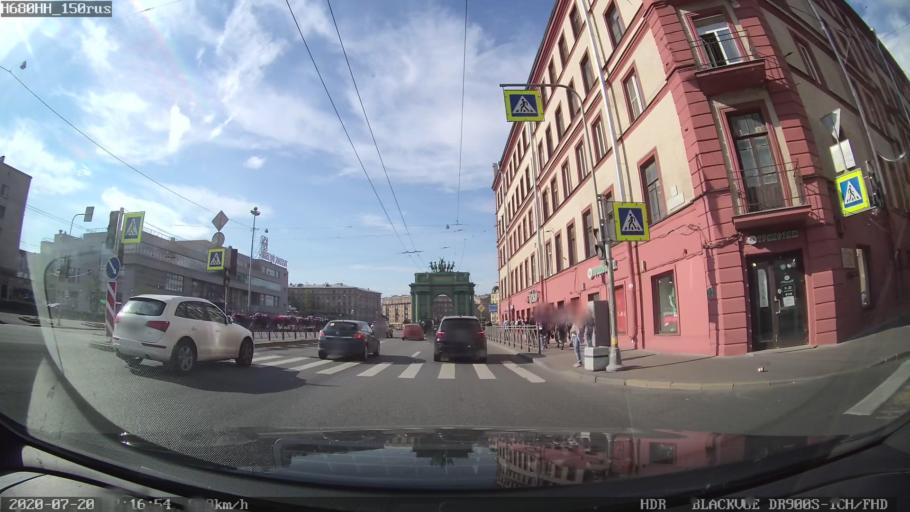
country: RU
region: St.-Petersburg
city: Admiralteisky
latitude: 59.8995
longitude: 30.2750
